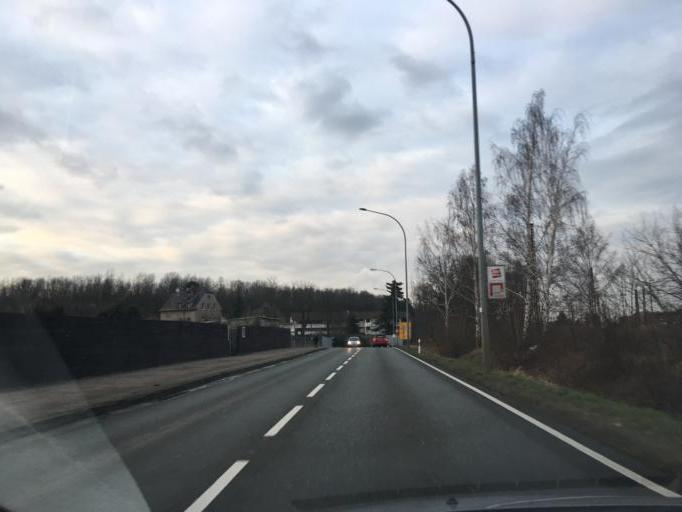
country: DE
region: Saxony
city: Borna
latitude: 51.1178
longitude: 12.4850
